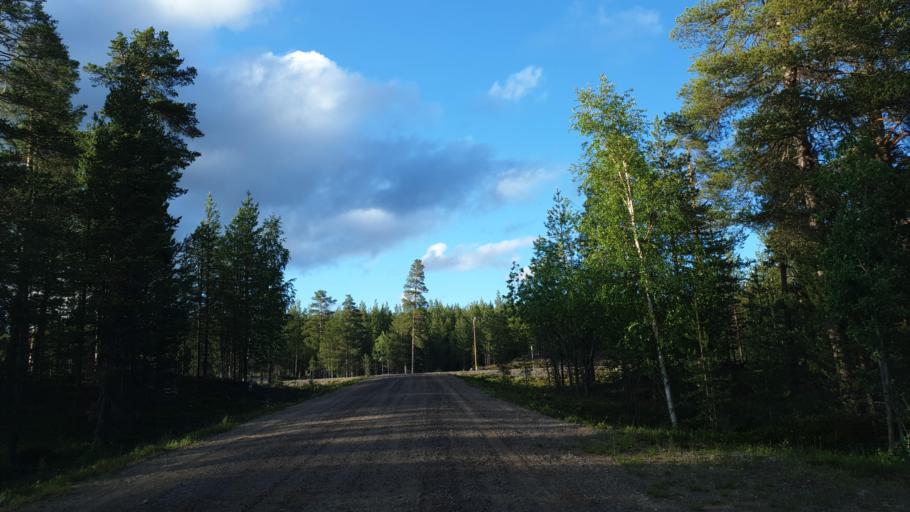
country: SE
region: Norrbotten
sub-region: Arvidsjaurs Kommun
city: Arvidsjaur
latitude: 65.7132
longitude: 18.7128
